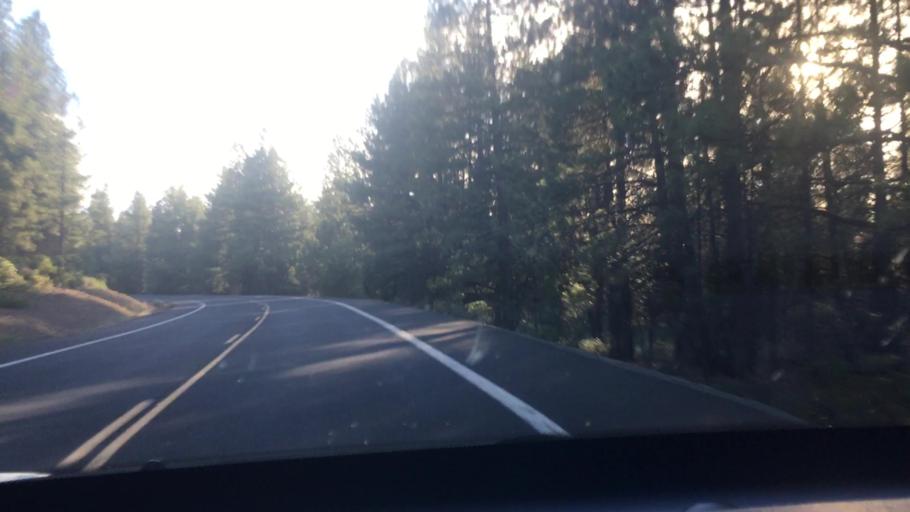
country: US
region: Oregon
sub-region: Deschutes County
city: Deschutes River Woods
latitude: 44.0433
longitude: -121.4117
